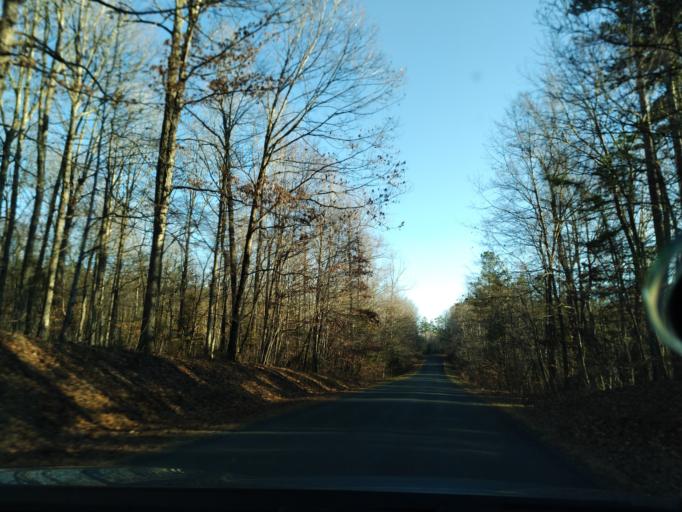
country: US
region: Virginia
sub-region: Appomattox County
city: Appomattox
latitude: 37.3873
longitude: -78.6549
